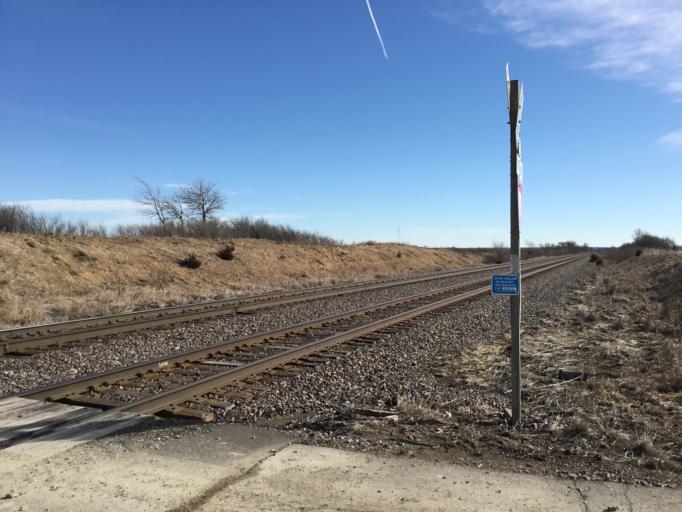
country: US
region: Kansas
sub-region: Morris County
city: Council Grove
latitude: 38.8555
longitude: -96.5393
